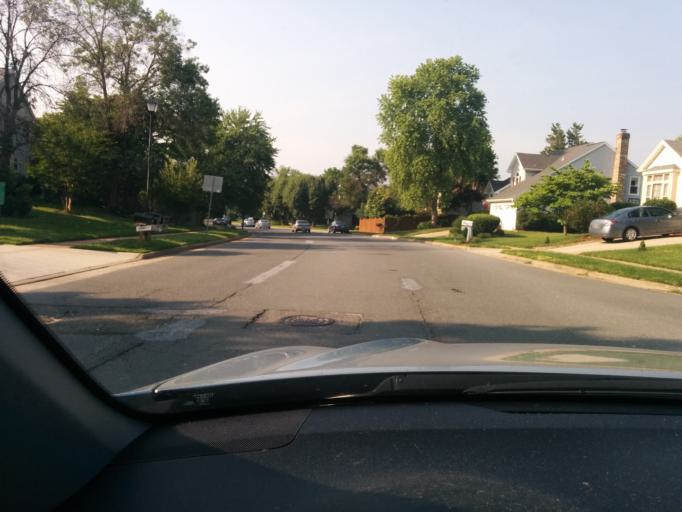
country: US
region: Virginia
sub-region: Fairfax County
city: Oak Hill
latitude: 38.9124
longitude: -77.4062
